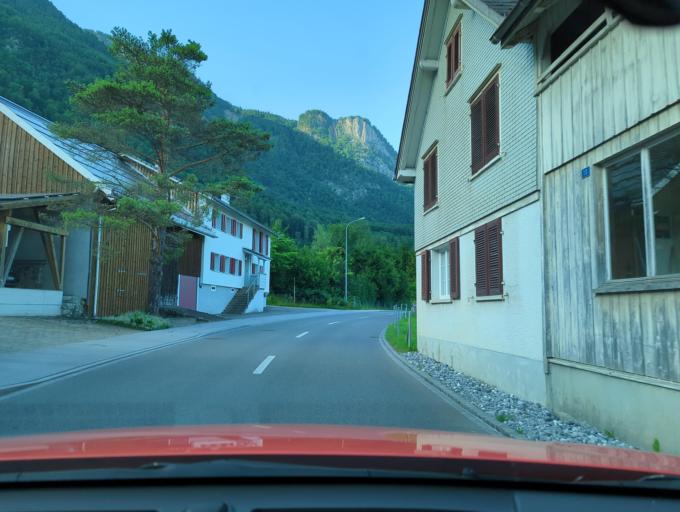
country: CH
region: Saint Gallen
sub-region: Wahlkreis Werdenberg
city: Sennwald
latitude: 47.2478
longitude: 9.4754
